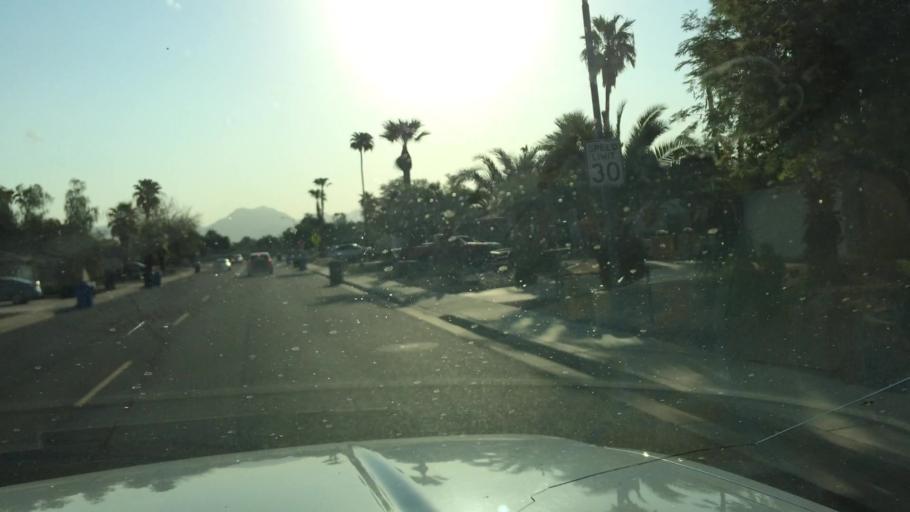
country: US
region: Arizona
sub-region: Maricopa County
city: Paradise Valley
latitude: 33.6191
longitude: -111.9543
